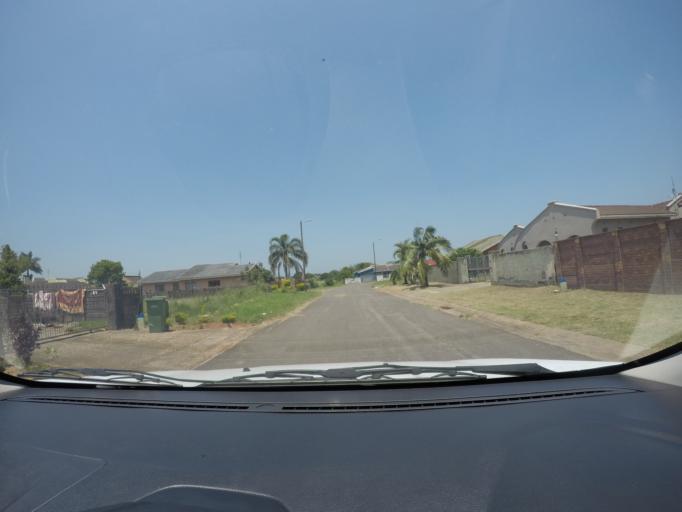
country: ZA
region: KwaZulu-Natal
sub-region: uThungulu District Municipality
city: eSikhawini
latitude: -28.8879
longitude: 31.8848
